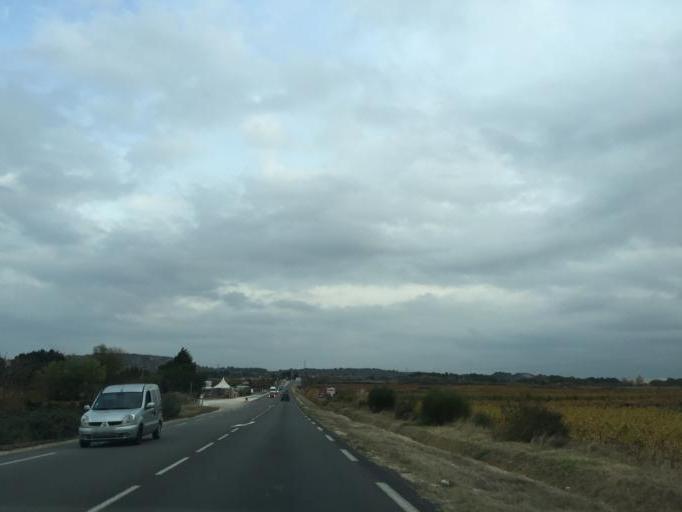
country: FR
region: Languedoc-Roussillon
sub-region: Departement du Gard
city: Remoulins
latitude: 43.9396
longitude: 4.5864
